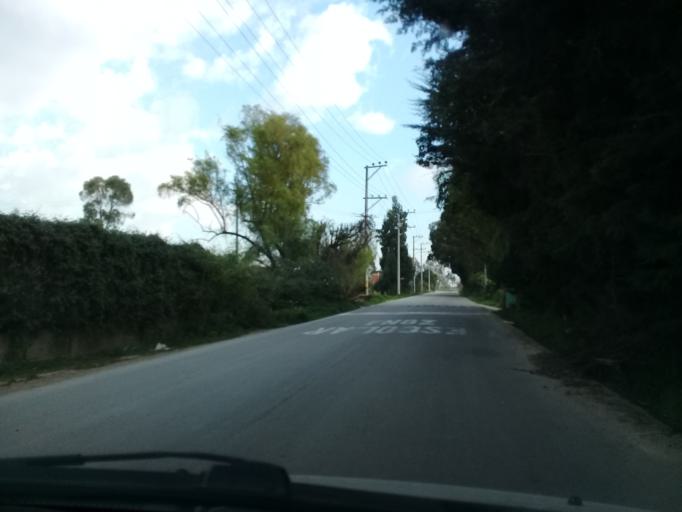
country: CO
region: Cundinamarca
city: Madrid
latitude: 4.7835
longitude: -74.2705
